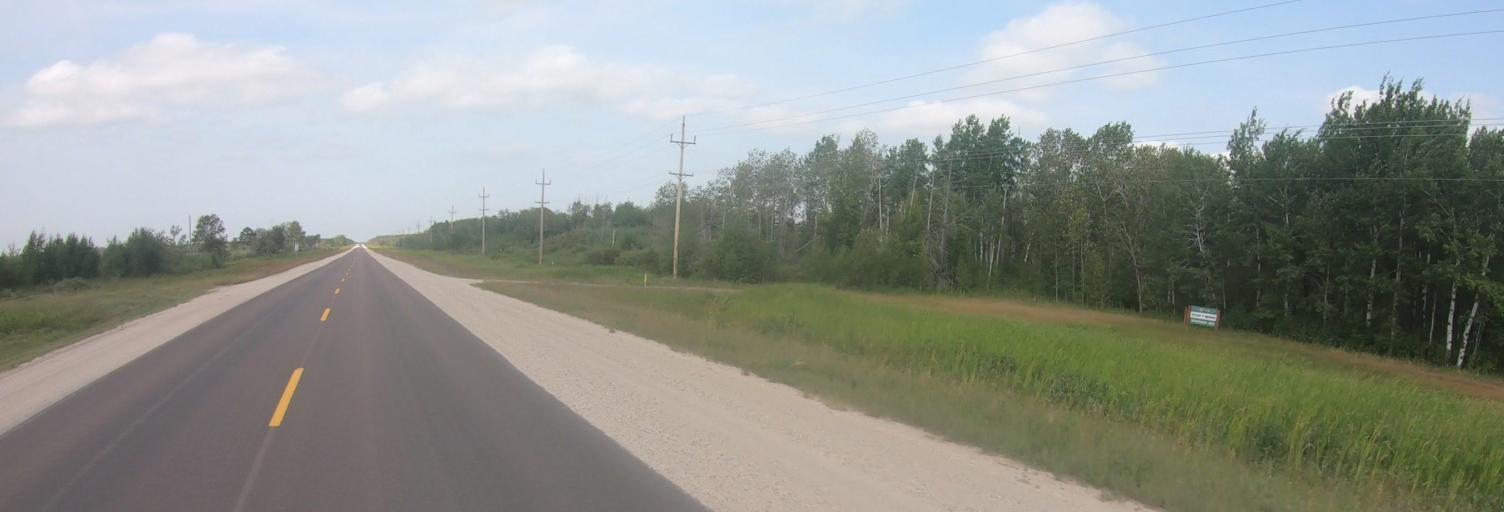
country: CA
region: Manitoba
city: La Broquerie
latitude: 49.2674
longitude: -96.3963
